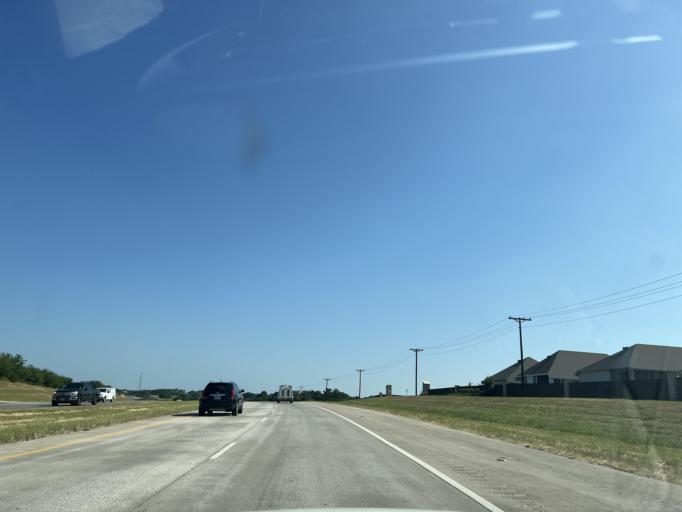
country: US
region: Texas
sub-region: Washington County
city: Brenham
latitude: 30.1727
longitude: -96.4251
